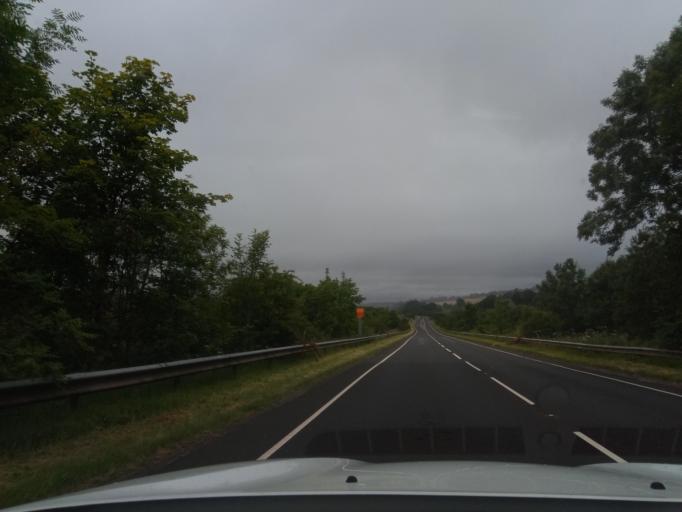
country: GB
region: Scotland
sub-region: The Scottish Borders
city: Earlston
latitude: 55.6687
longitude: -2.6953
